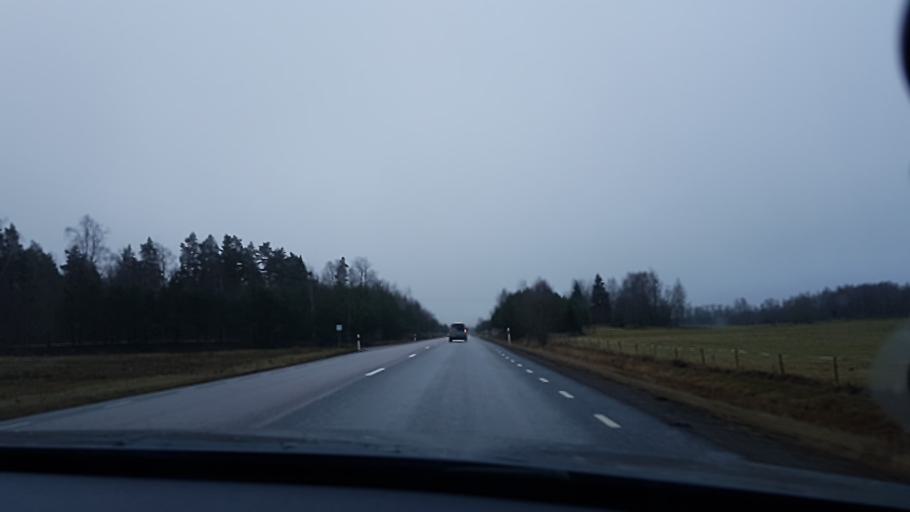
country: SE
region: Vaestra Goetaland
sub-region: Mariestads Kommun
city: Mariestad
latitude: 58.8056
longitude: 13.9753
